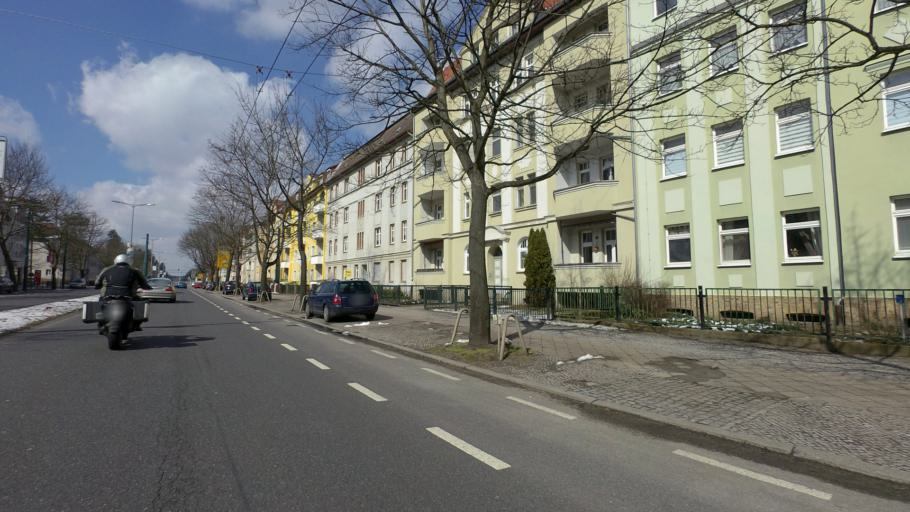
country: DE
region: Brandenburg
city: Eberswalde
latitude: 52.8370
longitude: 13.7856
